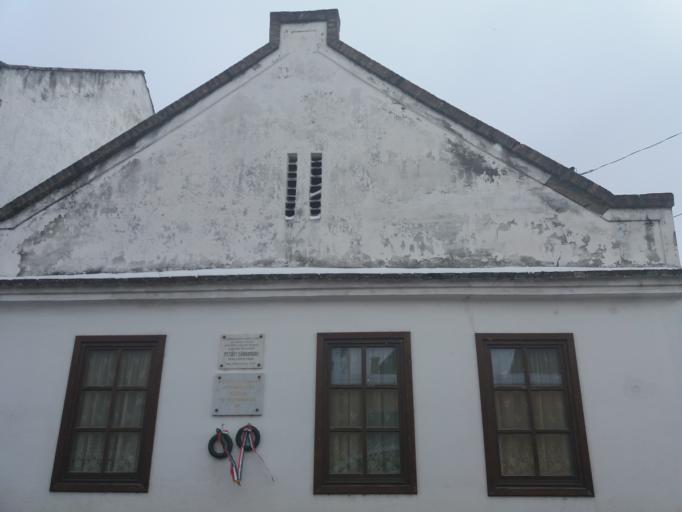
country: HU
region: Veszprem
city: Papa
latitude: 47.3261
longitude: 17.4655
